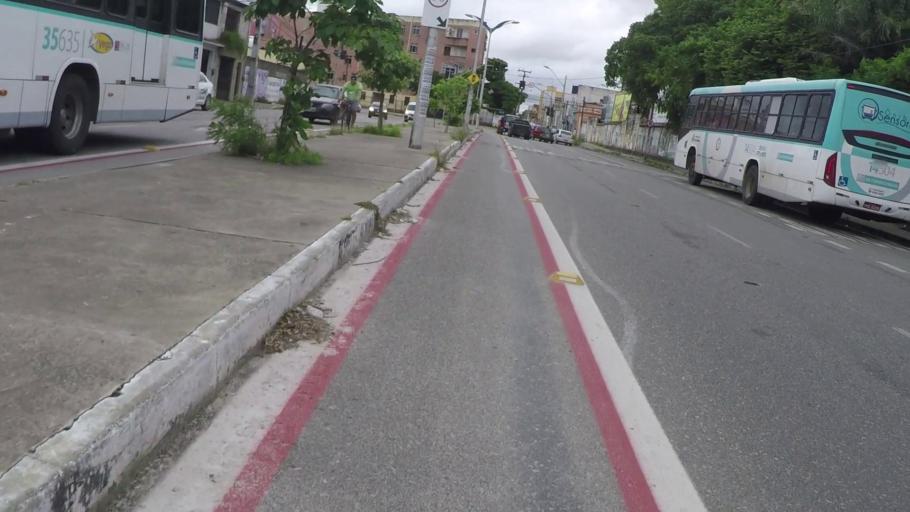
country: BR
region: Ceara
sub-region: Fortaleza
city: Fortaleza
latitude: -3.7321
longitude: -38.5427
